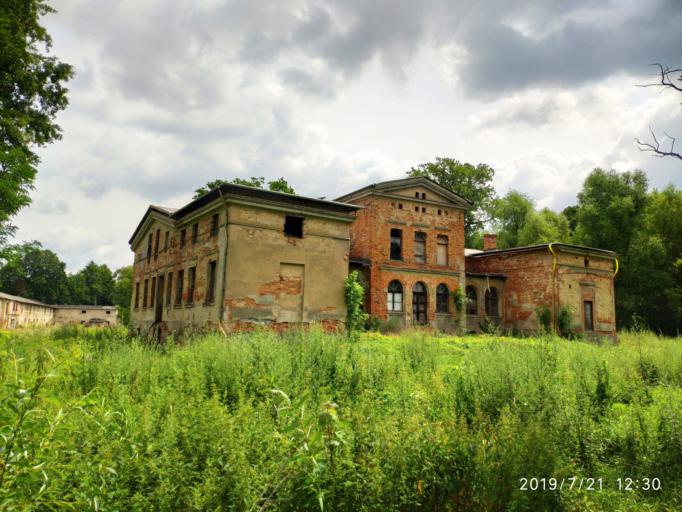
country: PL
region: Lubusz
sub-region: Powiat krosnienski
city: Dabie
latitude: 51.9561
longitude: 15.2470
